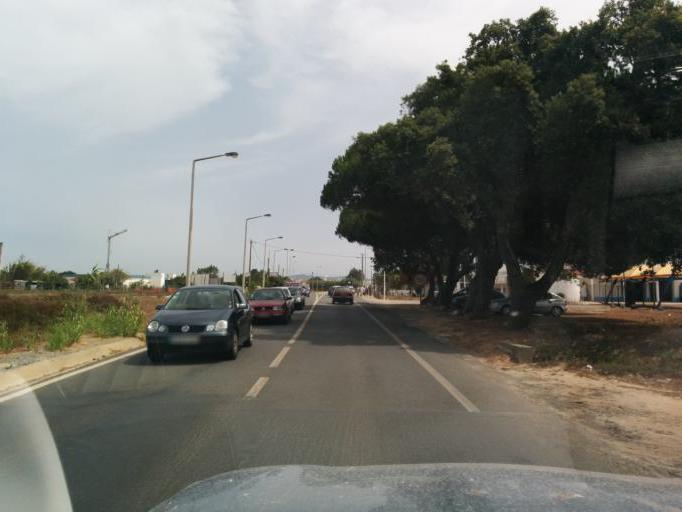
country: PT
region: Beja
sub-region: Odemira
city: Vila Nova de Milfontes
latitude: 37.7319
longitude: -8.7737
